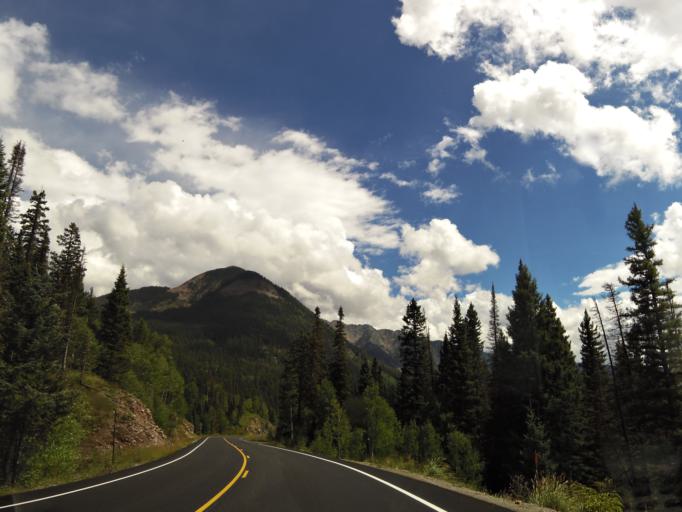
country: US
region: Colorado
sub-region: San Juan County
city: Silverton
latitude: 37.6777
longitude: -107.7956
